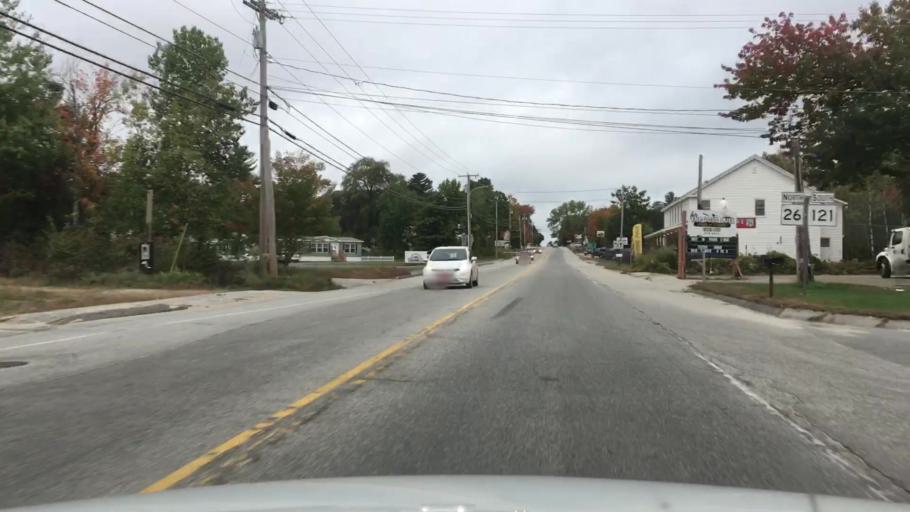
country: US
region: Maine
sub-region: Oxford County
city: Oxford
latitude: 44.1342
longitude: -70.4647
